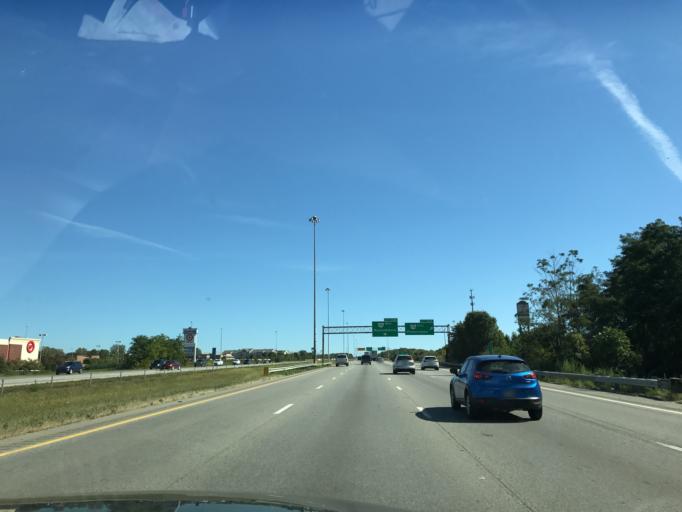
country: US
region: Ohio
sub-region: Franklin County
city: Reynoldsburg
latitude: 39.9323
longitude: -82.7942
